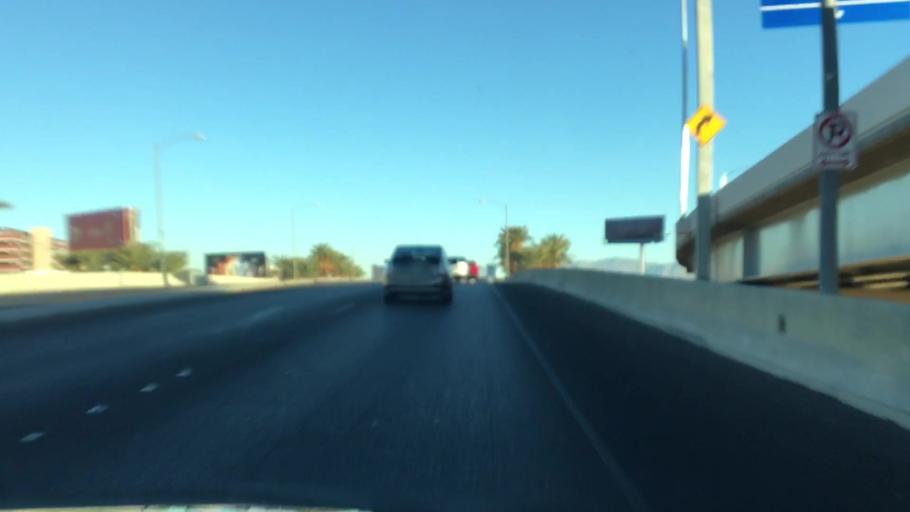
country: US
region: Nevada
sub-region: Clark County
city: Paradise
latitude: 36.0844
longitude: -115.1444
